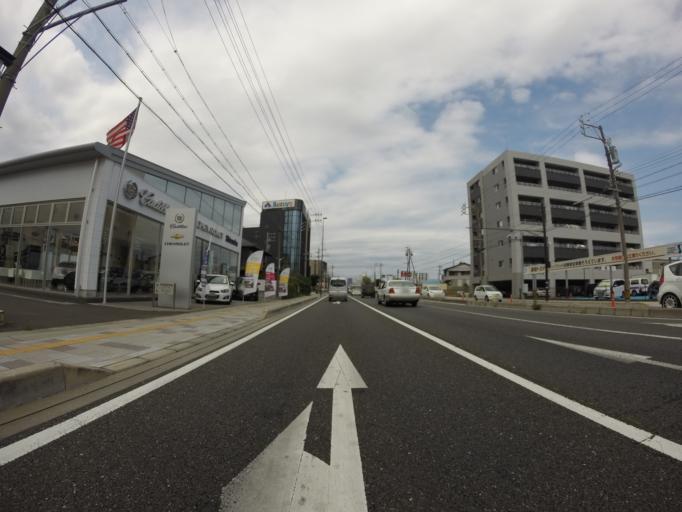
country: JP
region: Shizuoka
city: Shizuoka-shi
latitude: 34.9902
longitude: 138.4171
